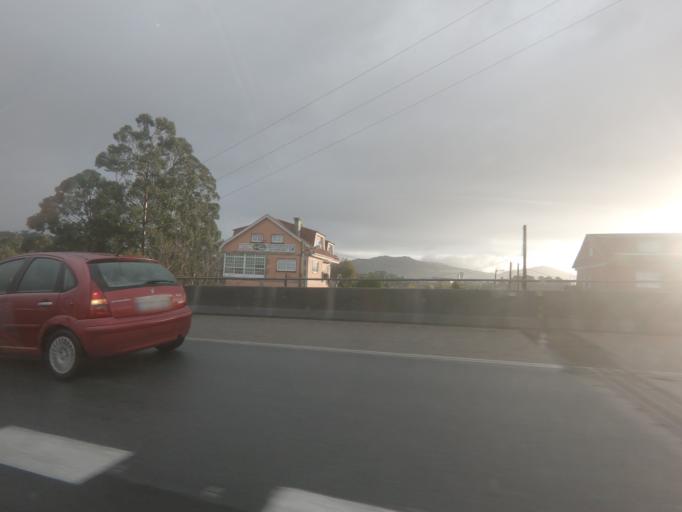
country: ES
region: Galicia
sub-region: Provincia de Pontevedra
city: Redondela
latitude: 42.2261
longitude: -8.6440
